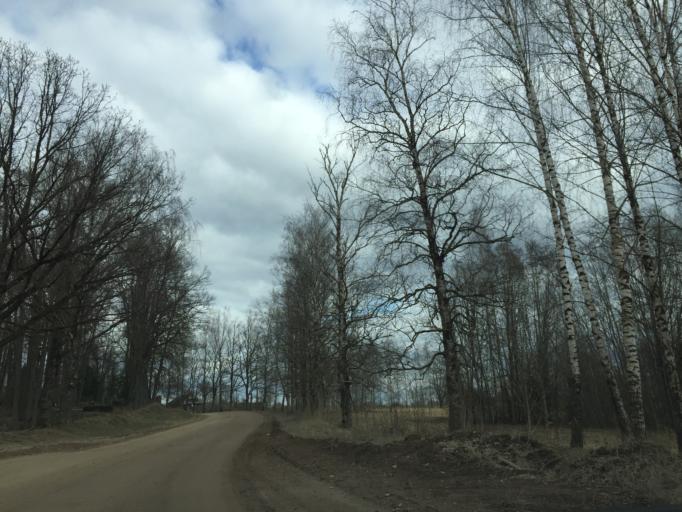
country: LV
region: Vecumnieki
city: Vecumnieki
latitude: 56.5044
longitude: 24.7169
